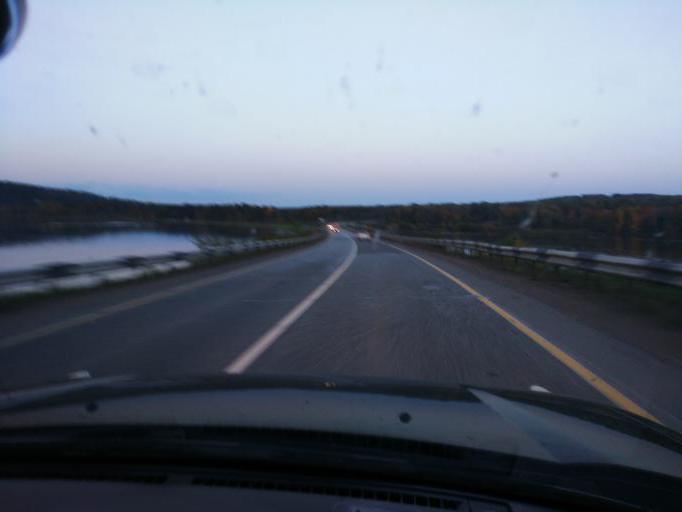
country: RU
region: Perm
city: Verkhnechusovskiye Gorodki
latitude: 58.2936
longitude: 56.8775
